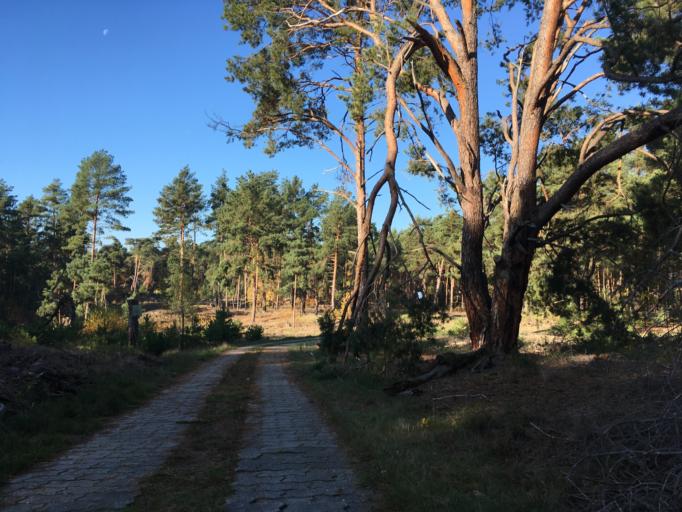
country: DE
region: Brandenburg
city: Wendisch Rietz
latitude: 52.1828
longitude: 14.0022
